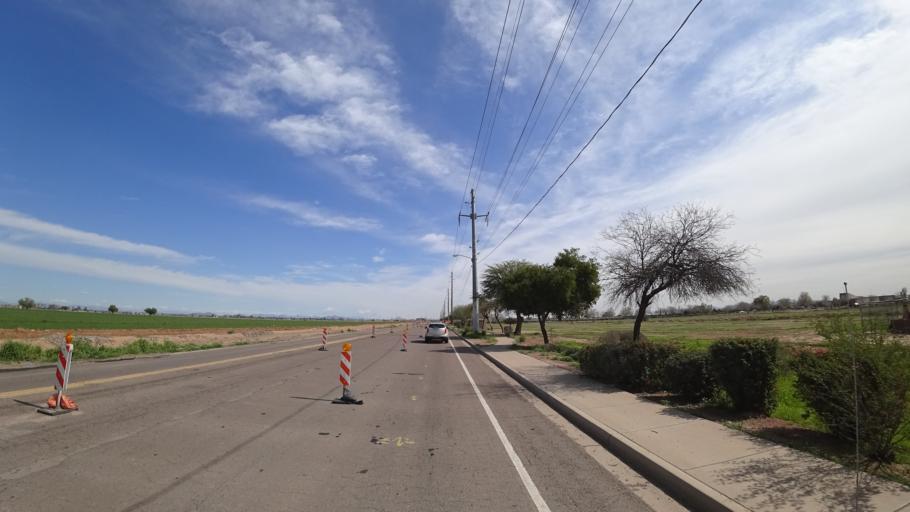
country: US
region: Arizona
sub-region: Maricopa County
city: Tolleson
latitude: 33.4791
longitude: -112.2802
